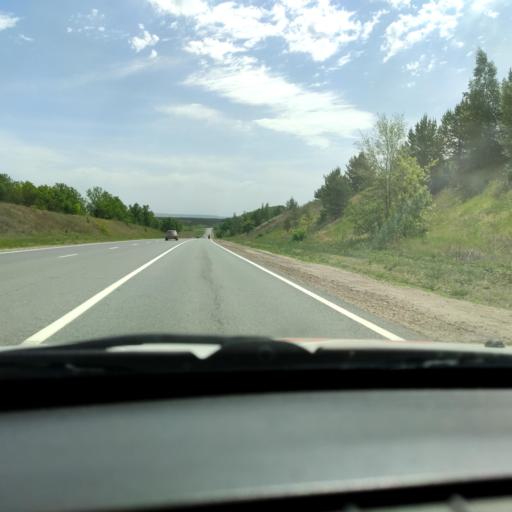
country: RU
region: Samara
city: Mirnyy
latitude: 53.5785
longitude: 50.2877
